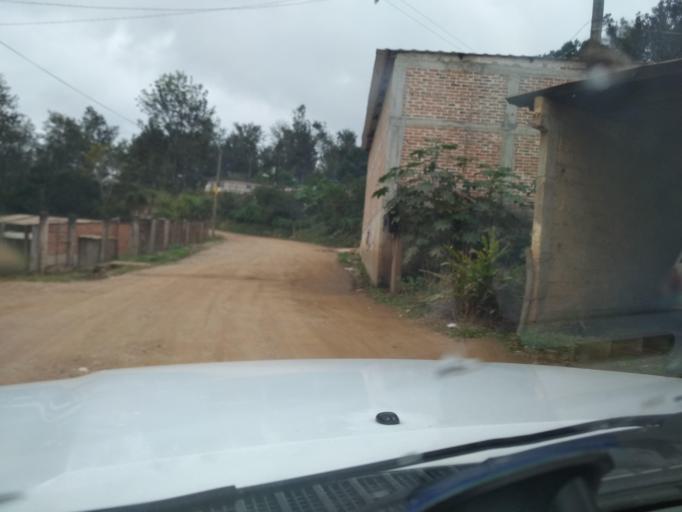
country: MX
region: Veracruz
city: El Castillo
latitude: 19.5437
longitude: -96.8316
